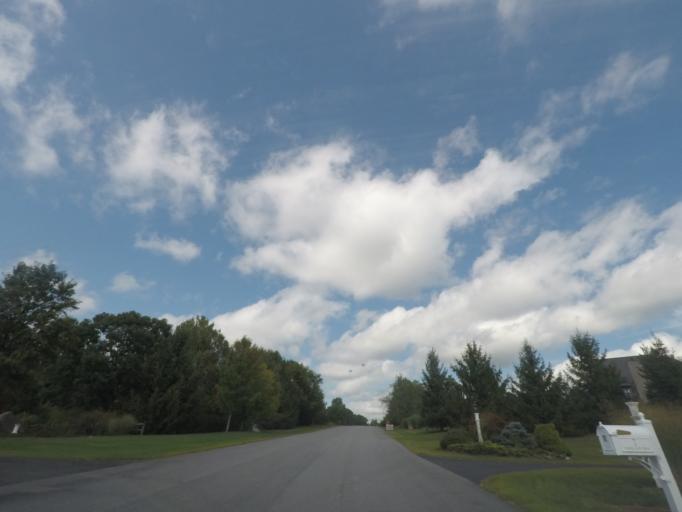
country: US
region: New York
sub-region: Rensselaer County
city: West Sand Lake
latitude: 42.5943
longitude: -73.6255
